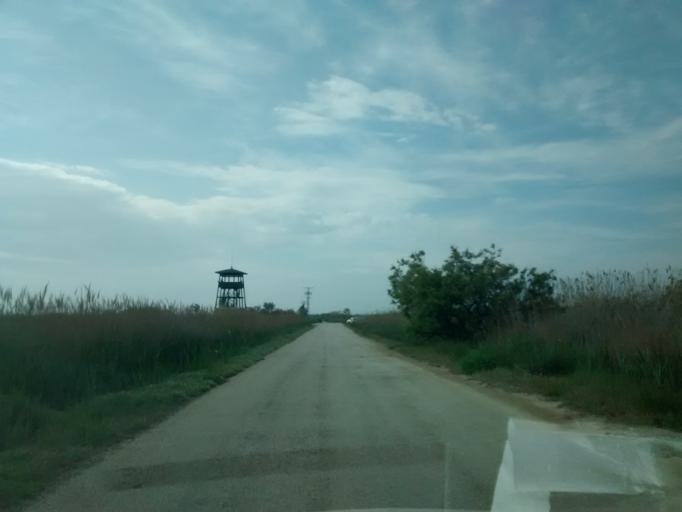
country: ES
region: Catalonia
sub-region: Provincia de Tarragona
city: Deltebre
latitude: 40.6862
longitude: 0.8512
